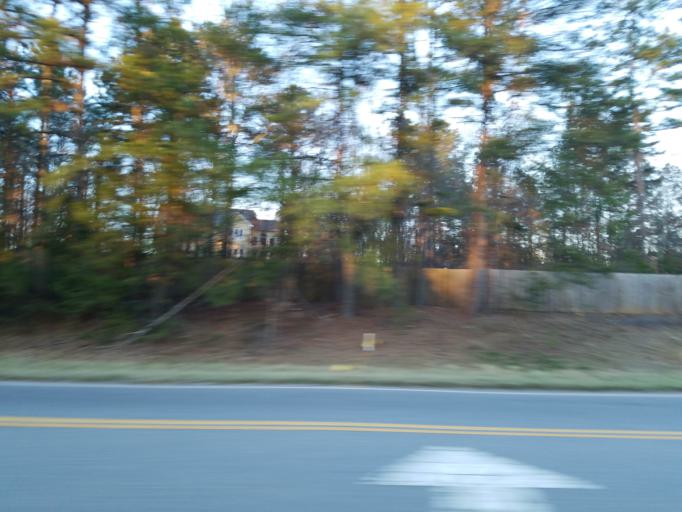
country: US
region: Georgia
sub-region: Hall County
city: Oakwood
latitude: 34.3170
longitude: -84.0009
